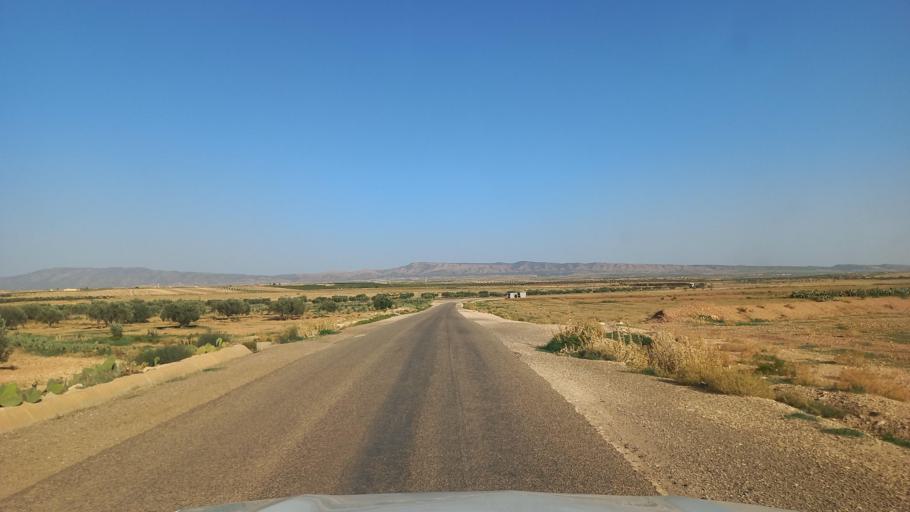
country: TN
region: Al Qasrayn
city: Sbiba
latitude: 35.3781
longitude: 9.0290
